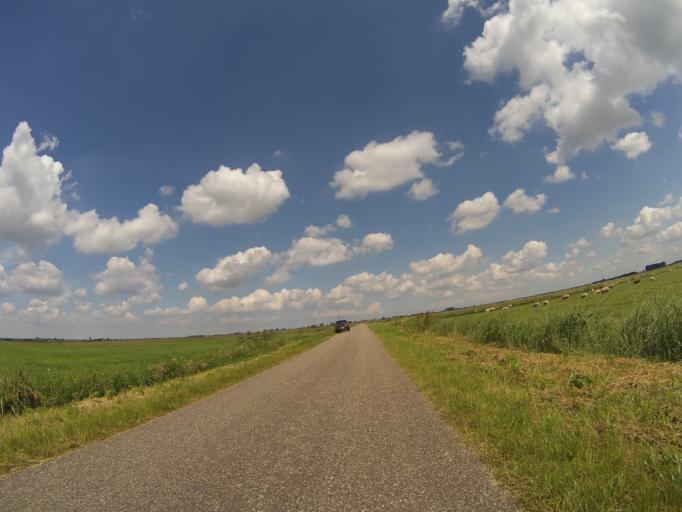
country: NL
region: Utrecht
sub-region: Gemeente Bunschoten
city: Spakenburg
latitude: 52.2373
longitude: 5.3319
